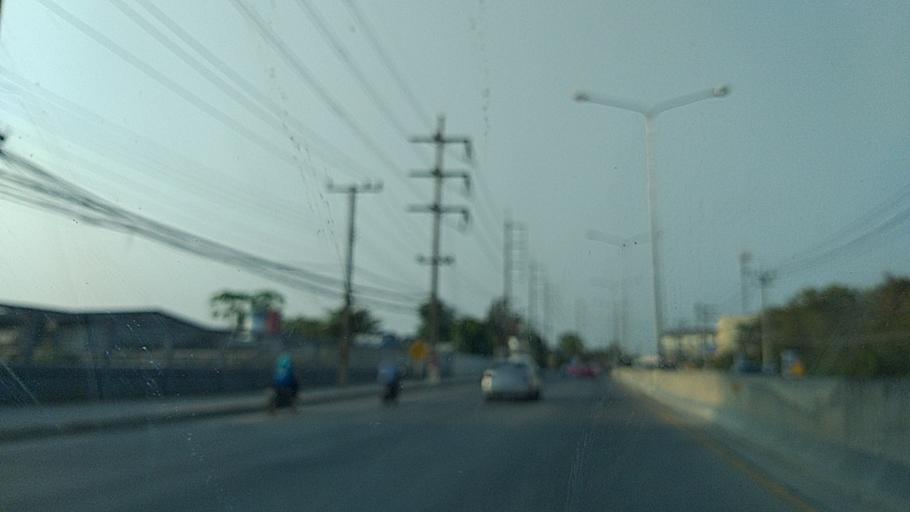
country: TH
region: Phra Nakhon Si Ayutthaya
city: Ban Bang Kadi Pathum Thani
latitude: 13.9911
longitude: 100.5506
